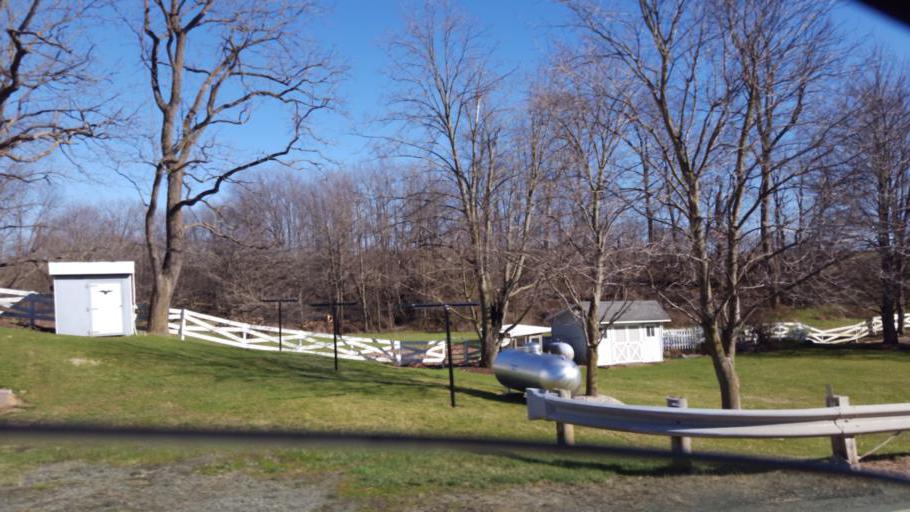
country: US
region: Ohio
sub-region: Wayne County
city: Dalton
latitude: 40.7095
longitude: -81.6978
